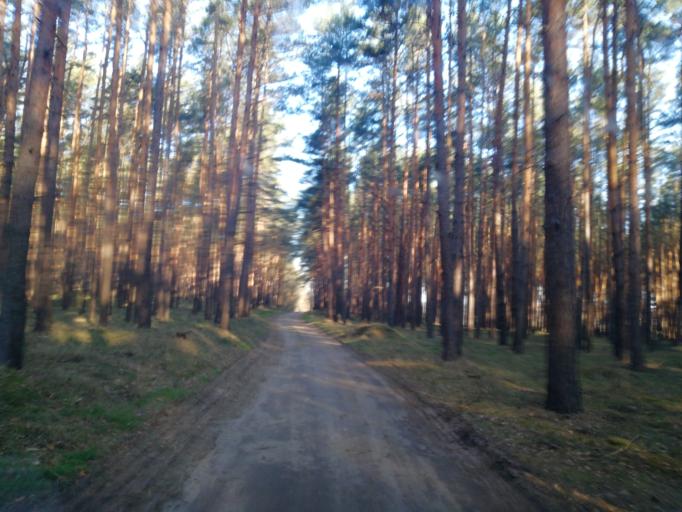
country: DE
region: Brandenburg
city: Drahnsdorf
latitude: 51.9464
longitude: 13.5647
